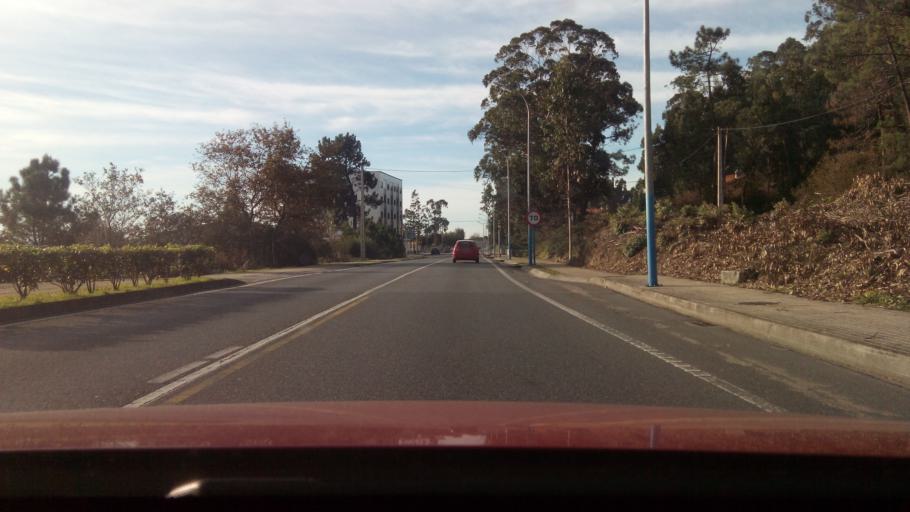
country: ES
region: Galicia
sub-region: Provincia de Pontevedra
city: O Grove
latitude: 42.4710
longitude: -8.8627
